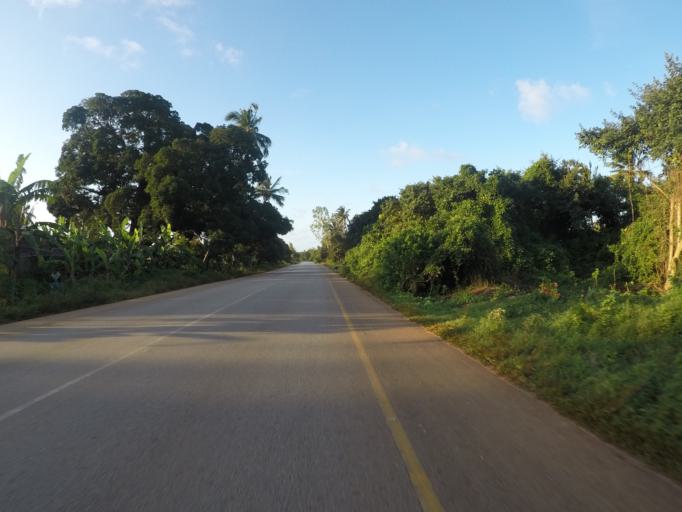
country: TZ
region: Zanzibar North
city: Kijini
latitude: -5.8524
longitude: 39.2827
